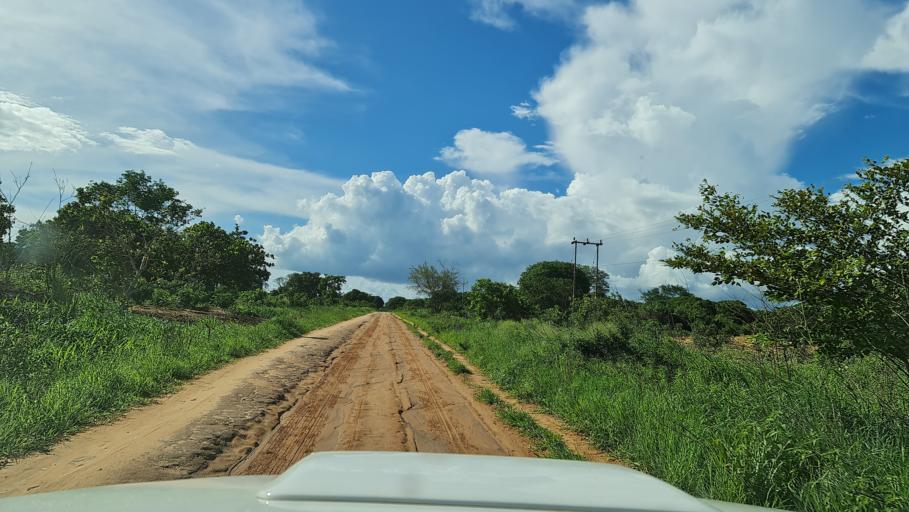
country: MZ
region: Nampula
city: Ilha de Mocambique
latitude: -15.2963
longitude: 40.1230
